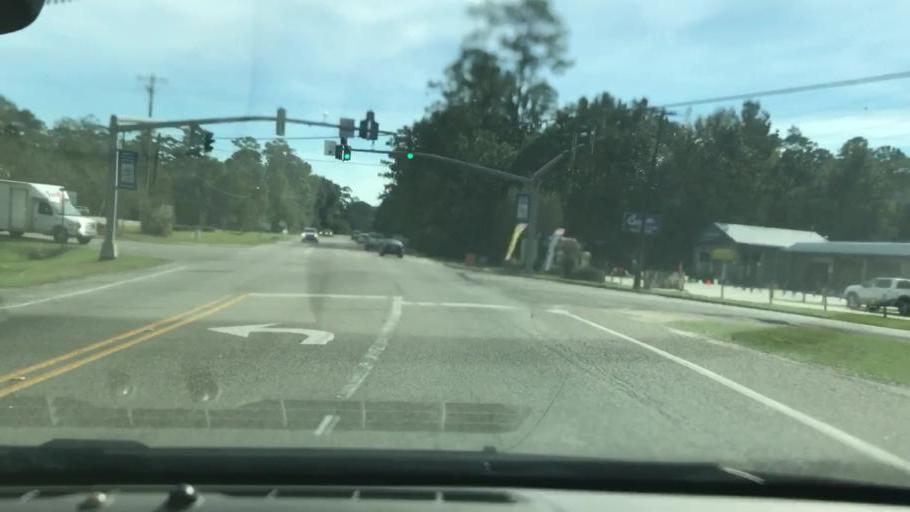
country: US
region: Louisiana
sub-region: Saint Tammany Parish
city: Pearl River
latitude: 30.3729
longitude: -89.7663
